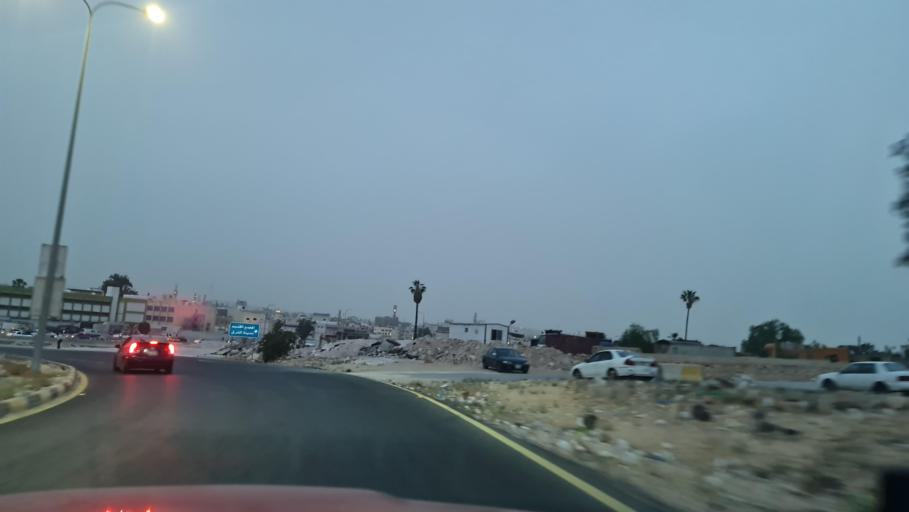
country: JO
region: Zarqa
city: Zarqa
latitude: 32.0564
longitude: 36.0966
